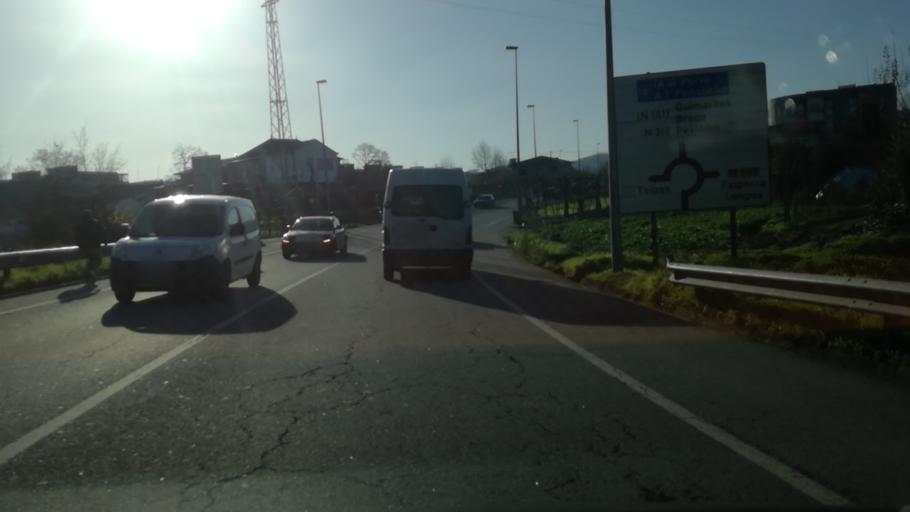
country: PT
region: Braga
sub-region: Guimaraes
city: Ponte
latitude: 41.4892
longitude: -8.3435
